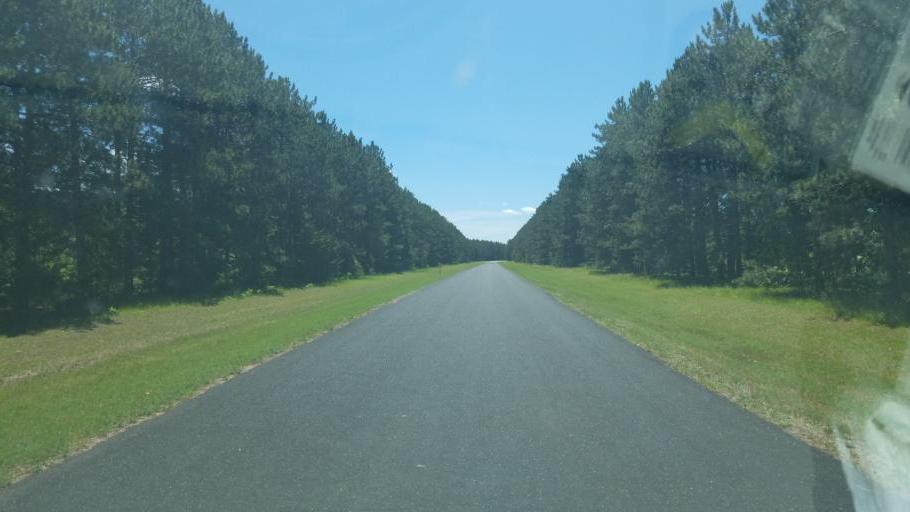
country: US
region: Wisconsin
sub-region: Juneau County
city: New Lisbon
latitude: 44.0510
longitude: -90.0283
